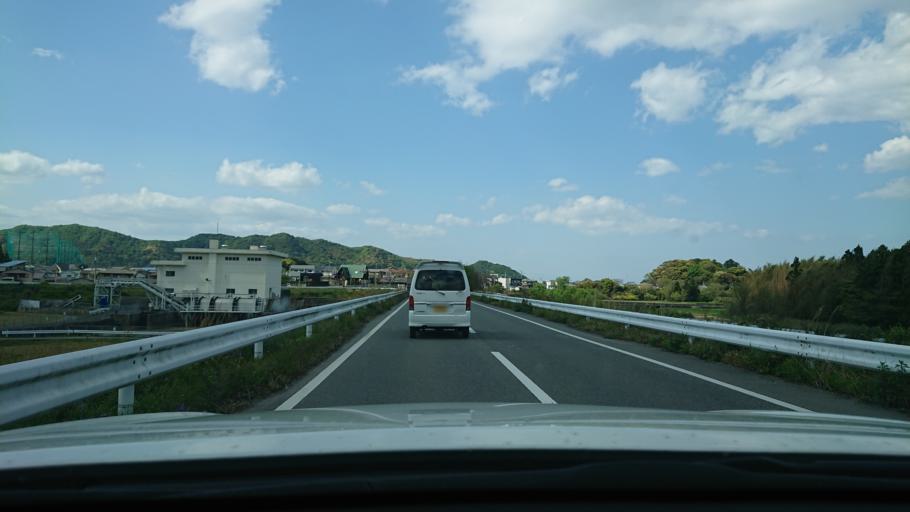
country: JP
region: Tokushima
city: Komatsushimacho
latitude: 33.9987
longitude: 134.5475
